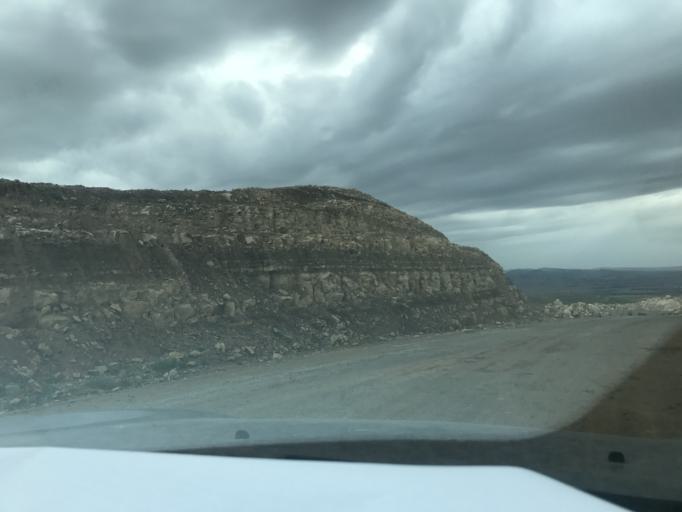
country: TN
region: Silyanah
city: Siliana
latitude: 36.0879
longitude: 9.4593
